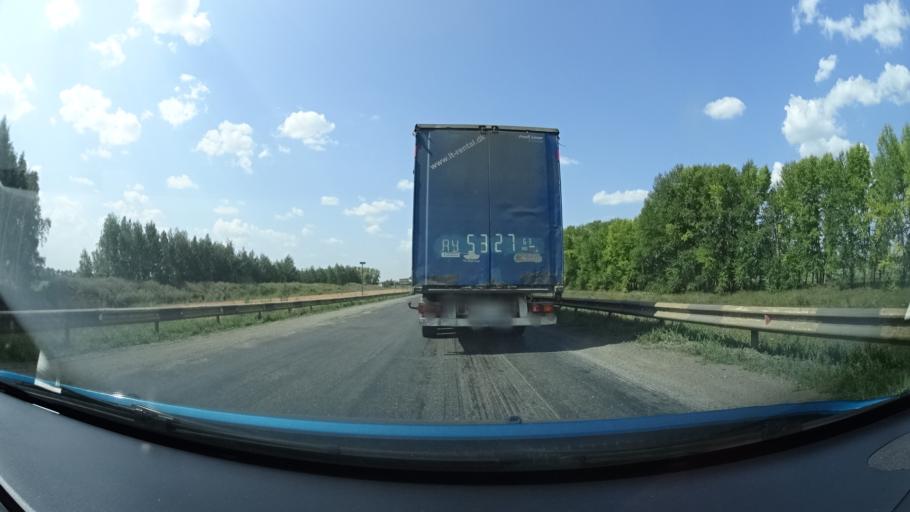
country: RU
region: Bashkortostan
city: Buzdyak
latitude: 54.6590
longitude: 54.6603
